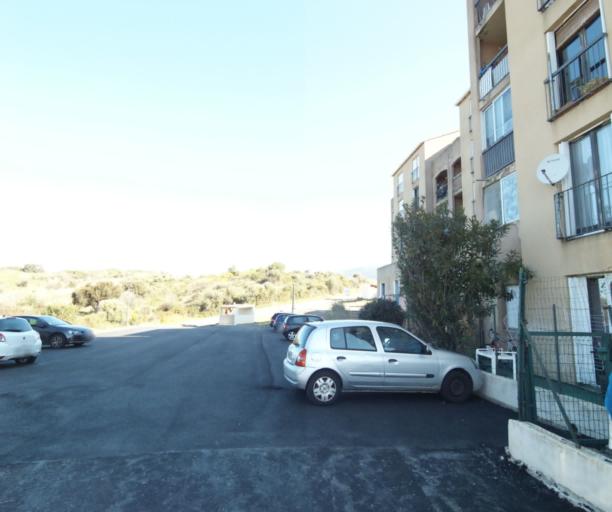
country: FR
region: Corsica
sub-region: Departement de la Corse-du-Sud
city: Propriano
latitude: 41.6688
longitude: 8.8971
